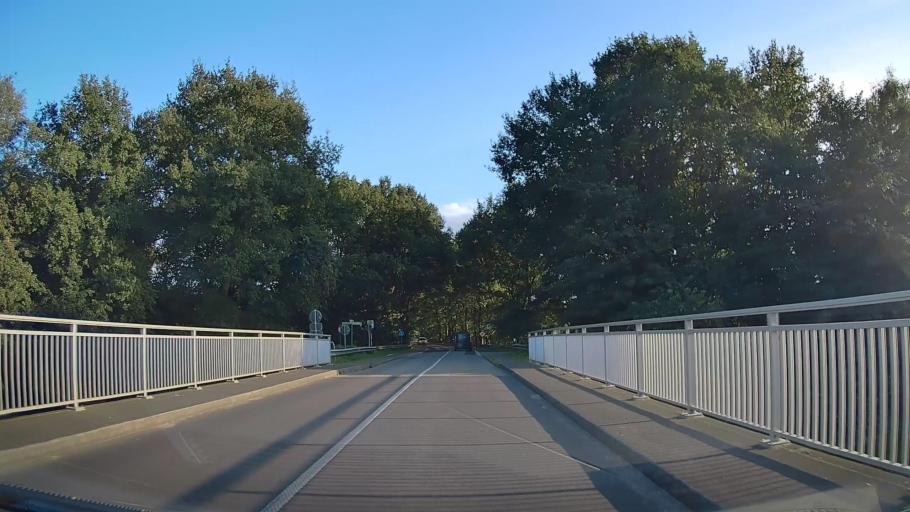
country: DE
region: Lower Saxony
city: Hilkenbrook
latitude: 53.0265
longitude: 7.7476
